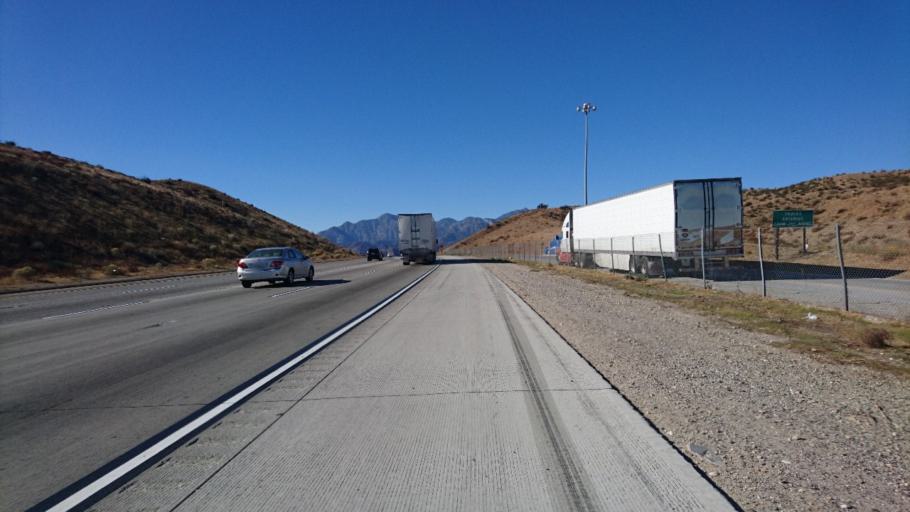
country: US
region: California
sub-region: San Bernardino County
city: Oak Hills
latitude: 34.3501
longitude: -117.4461
